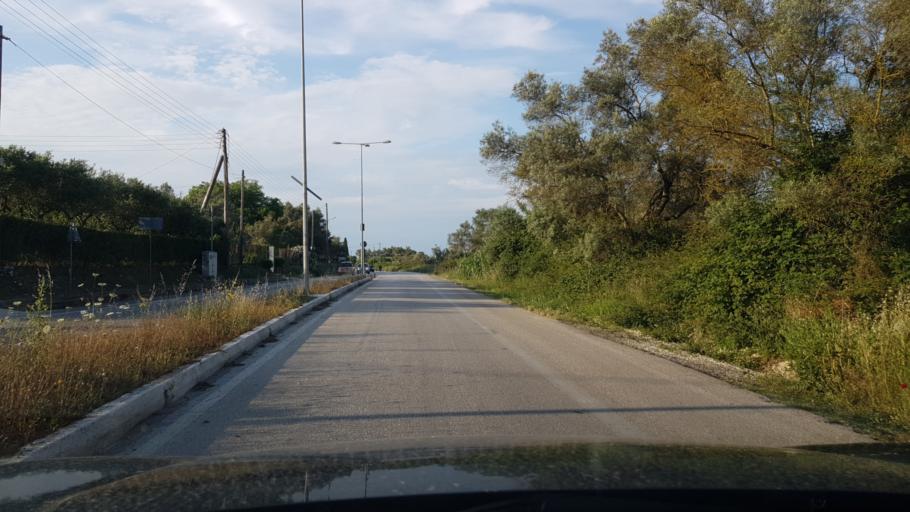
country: GR
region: Ionian Islands
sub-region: Lefkada
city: Lefkada
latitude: 38.8056
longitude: 20.7151
